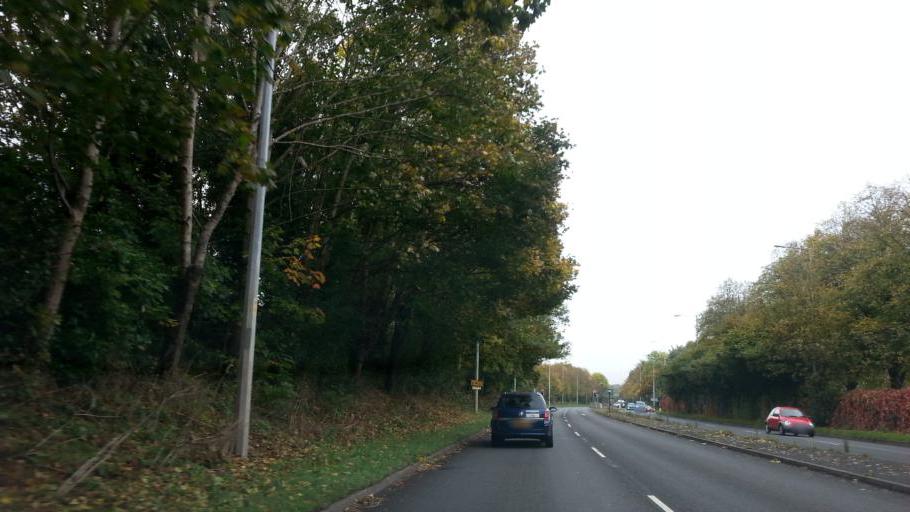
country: GB
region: England
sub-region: Worcestershire
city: Bromsgrove
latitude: 52.3287
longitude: -2.0547
